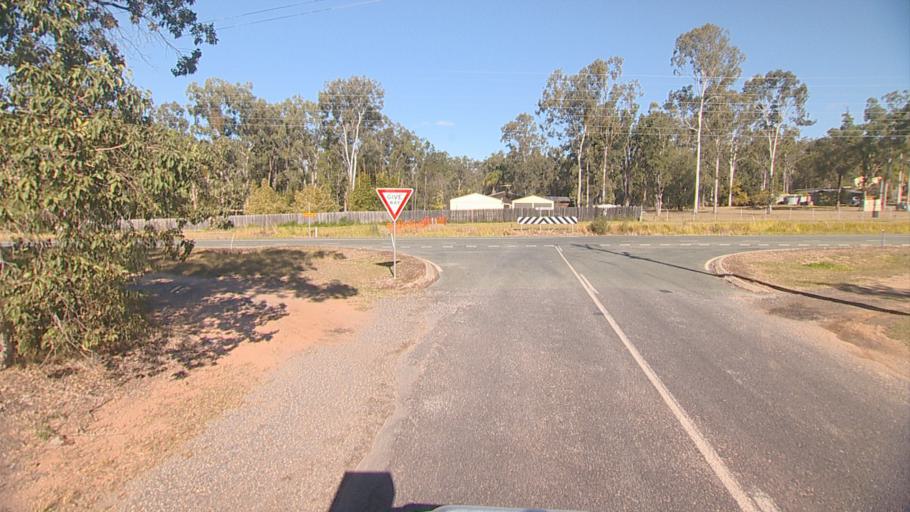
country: AU
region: Queensland
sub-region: Logan
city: Chambers Flat
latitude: -27.8040
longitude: 153.0713
